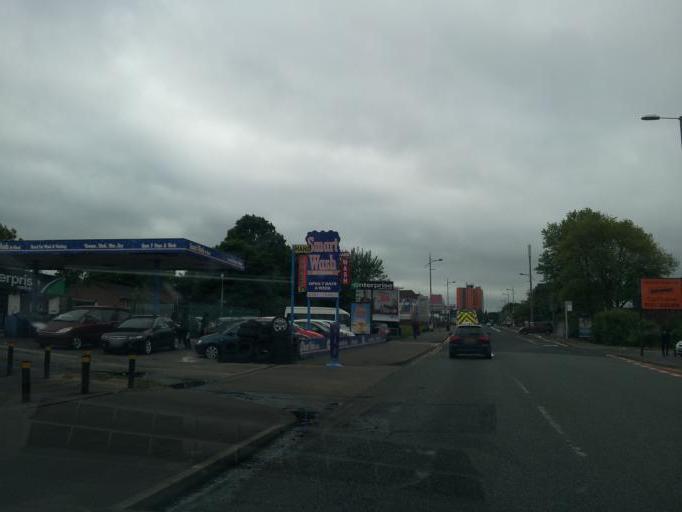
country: GB
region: England
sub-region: Manchester
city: Cheetham Hill
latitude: 53.4985
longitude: -2.2547
